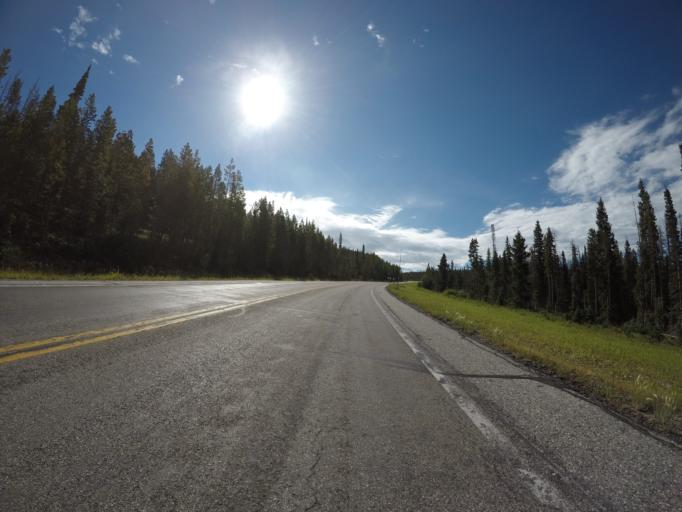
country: US
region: Wyoming
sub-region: Carbon County
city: Saratoga
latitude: 41.3252
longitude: -106.4633
